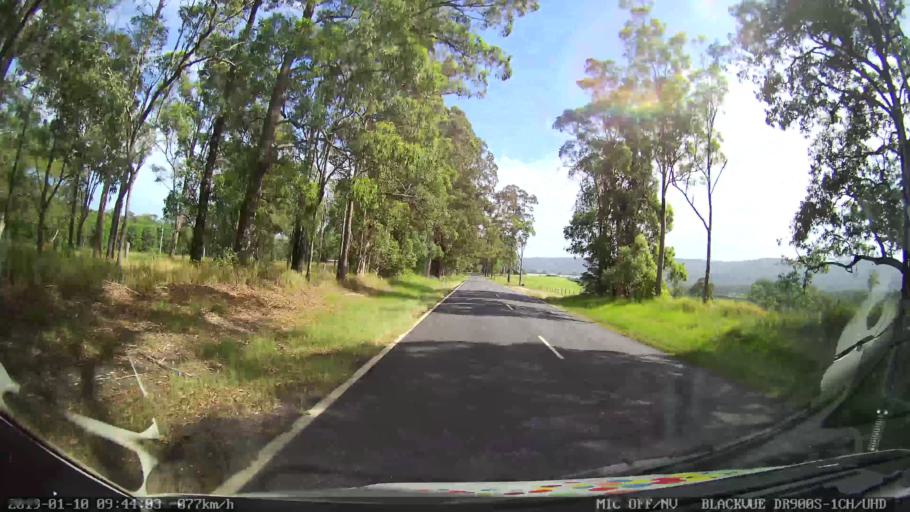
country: AU
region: New South Wales
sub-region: Coffs Harbour
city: Nana Glen
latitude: -30.1214
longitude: 153.0033
